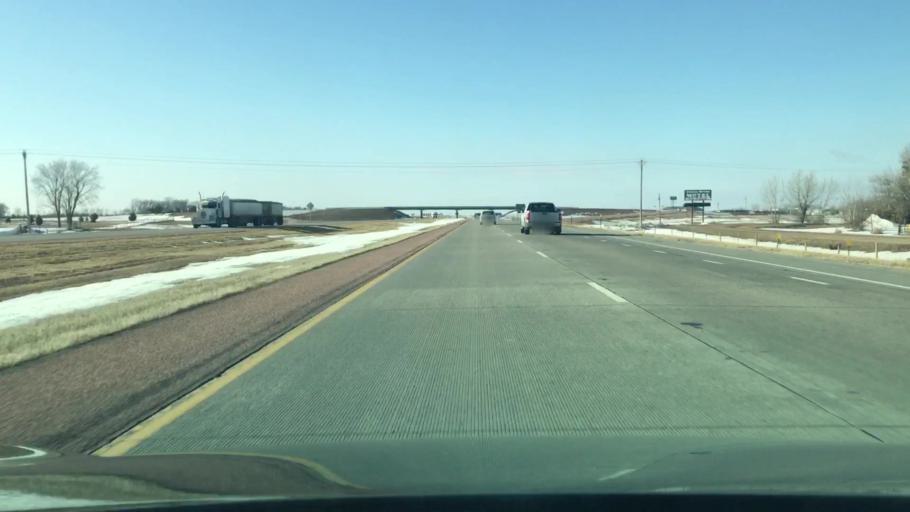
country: US
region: South Dakota
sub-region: Aurora County
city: Plankinton
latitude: 43.7031
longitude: -98.4798
